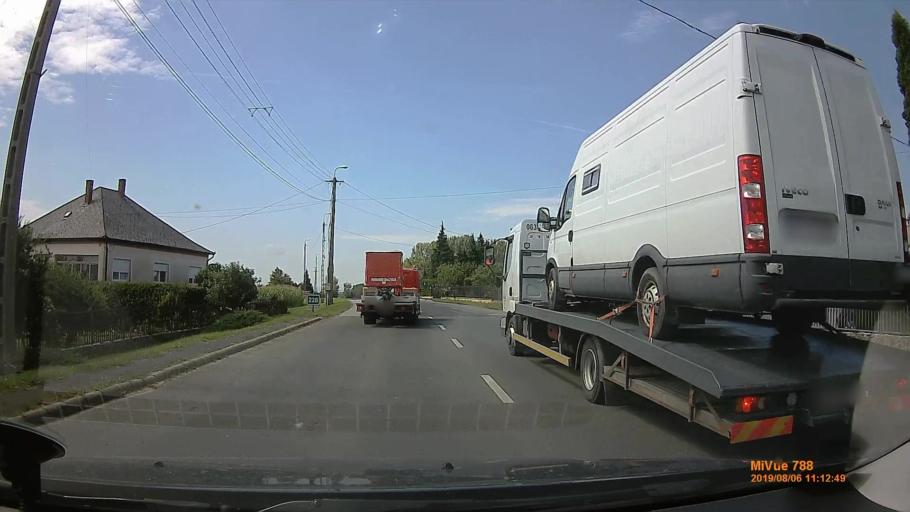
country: HU
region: Zala
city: Becsehely
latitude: 46.4452
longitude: 16.7685
